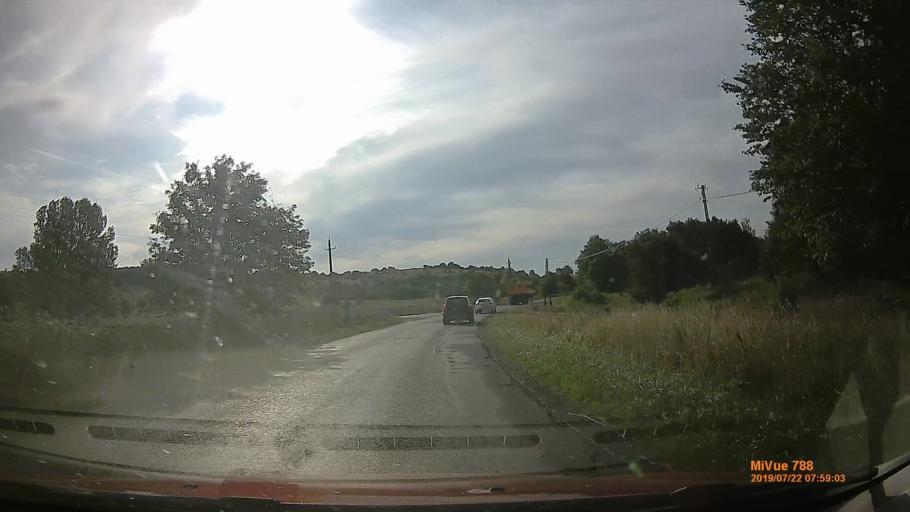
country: HU
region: Veszprem
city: Urkut
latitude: 47.0054
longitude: 17.6045
